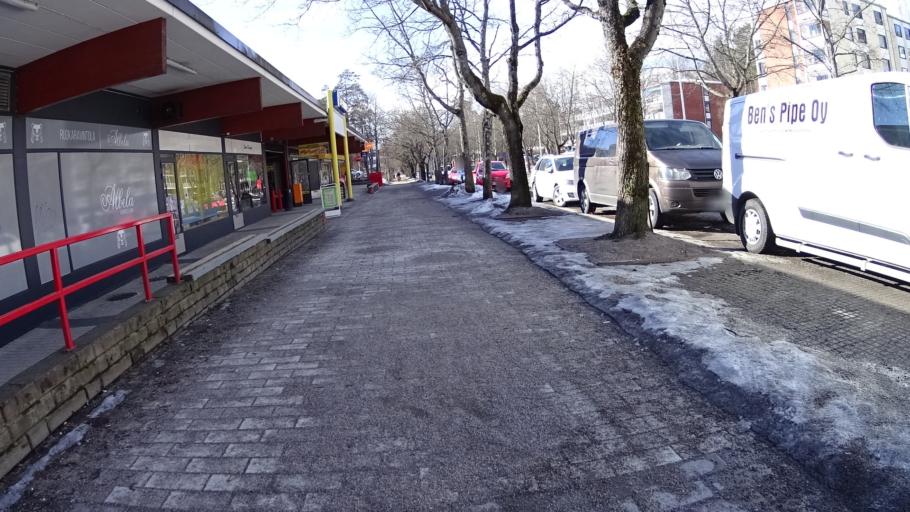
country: FI
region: Uusimaa
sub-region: Helsinki
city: Kilo
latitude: 60.2625
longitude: 24.8047
